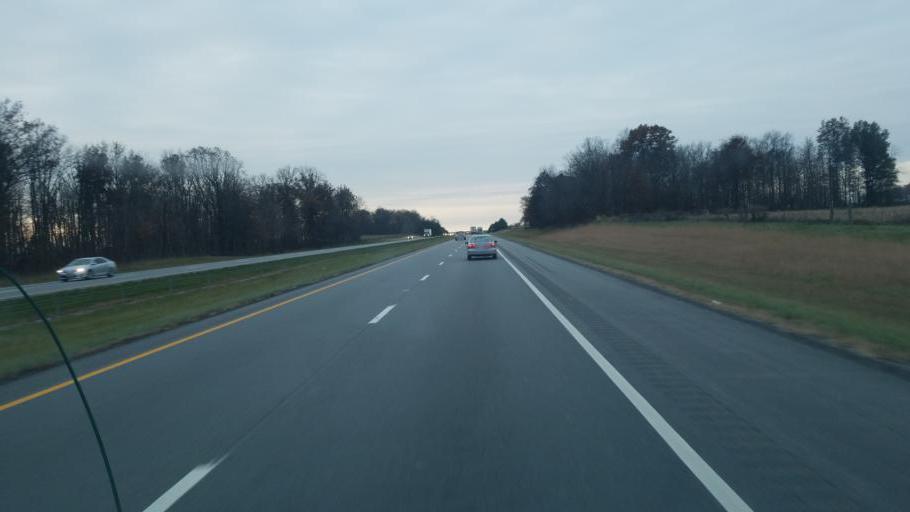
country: US
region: Ohio
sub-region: Auglaize County
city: Cridersville
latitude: 40.6150
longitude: -84.1483
